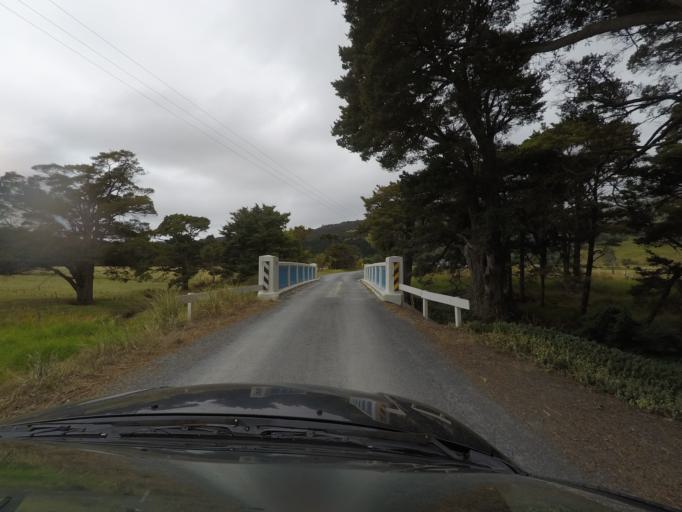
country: NZ
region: Auckland
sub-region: Auckland
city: Warkworth
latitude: -36.2619
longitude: 174.7264
